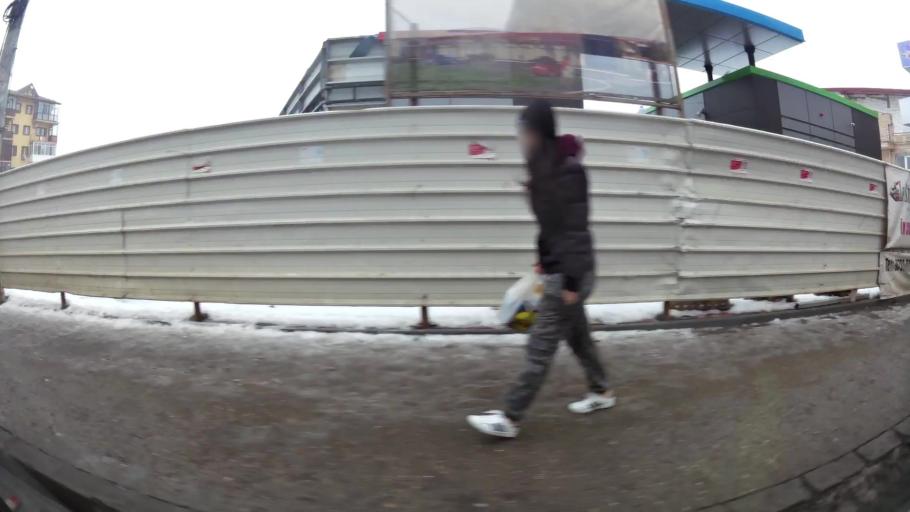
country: RO
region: Ilfov
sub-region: Comuna Chiajna
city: Chiajna
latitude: 44.4461
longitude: 25.9873
